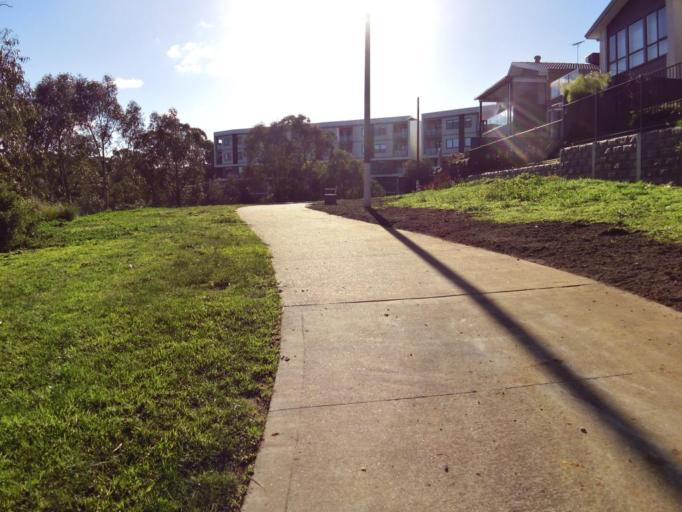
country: AU
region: Victoria
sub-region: Whittlesea
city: Mill Park
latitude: -37.6817
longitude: 145.0772
